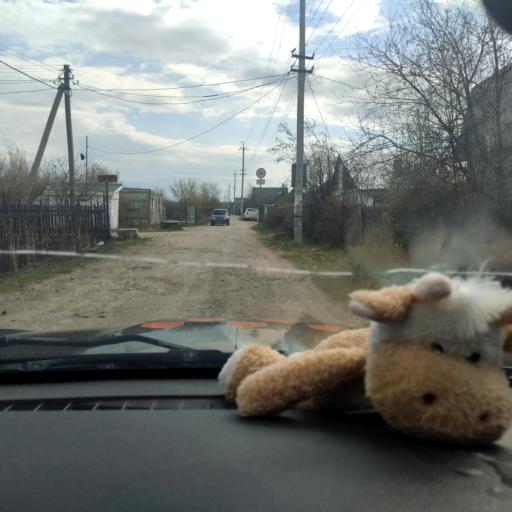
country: RU
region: Samara
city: Podstepki
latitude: 53.5924
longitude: 49.2244
